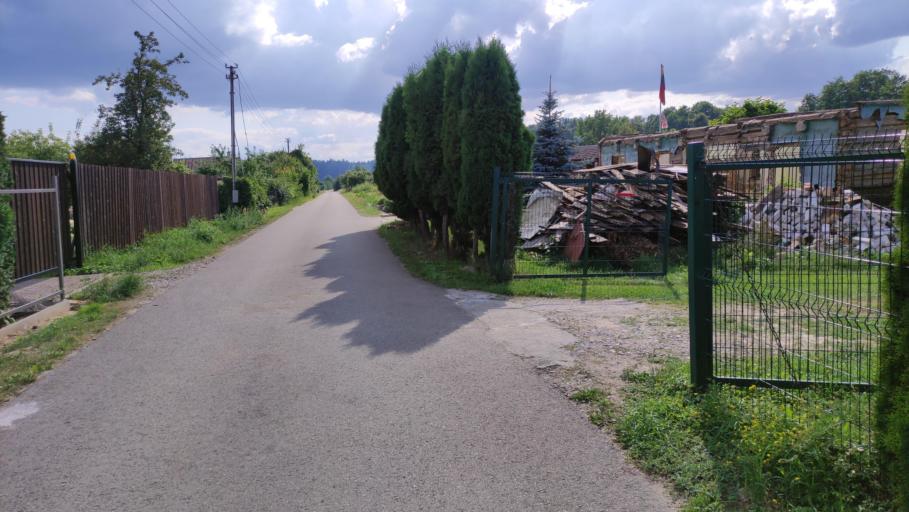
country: LT
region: Alytaus apskritis
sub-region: Alytus
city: Alytus
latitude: 54.4322
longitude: 24.0689
